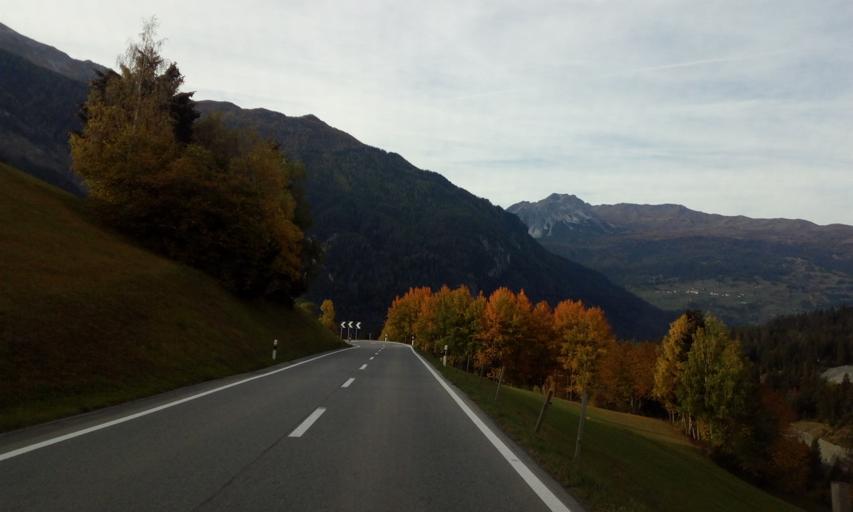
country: CH
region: Grisons
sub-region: Albula District
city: Tiefencastel
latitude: 46.6740
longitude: 9.6363
